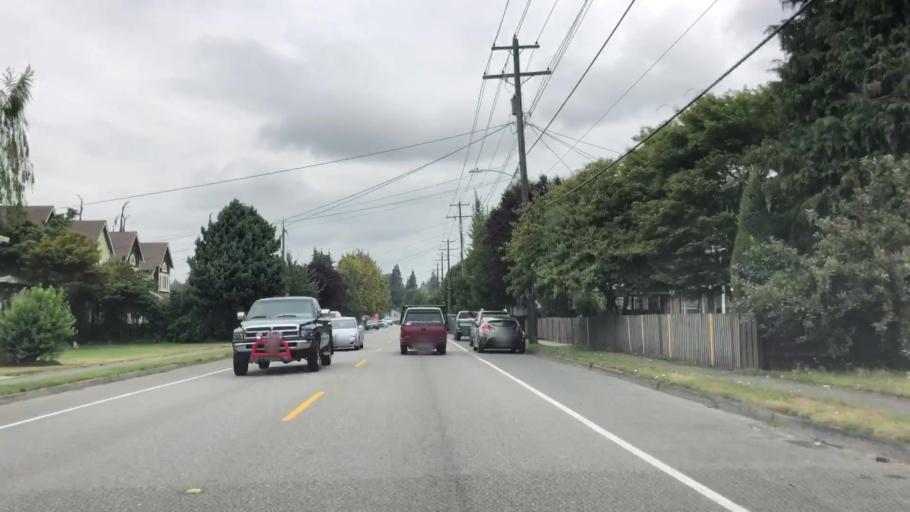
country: US
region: Washington
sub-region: Snohomish County
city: Snohomish
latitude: 47.9159
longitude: -122.0860
